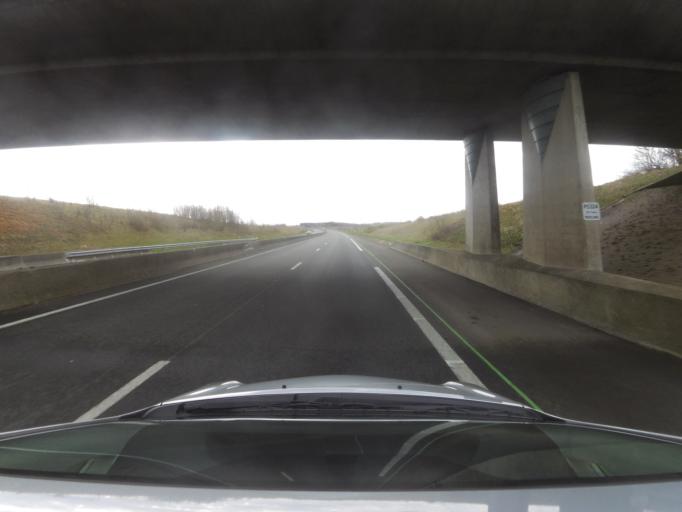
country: FR
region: Nord-Pas-de-Calais
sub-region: Departement du Pas-de-Calais
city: Saint-Josse
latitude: 50.4504
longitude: 1.6947
